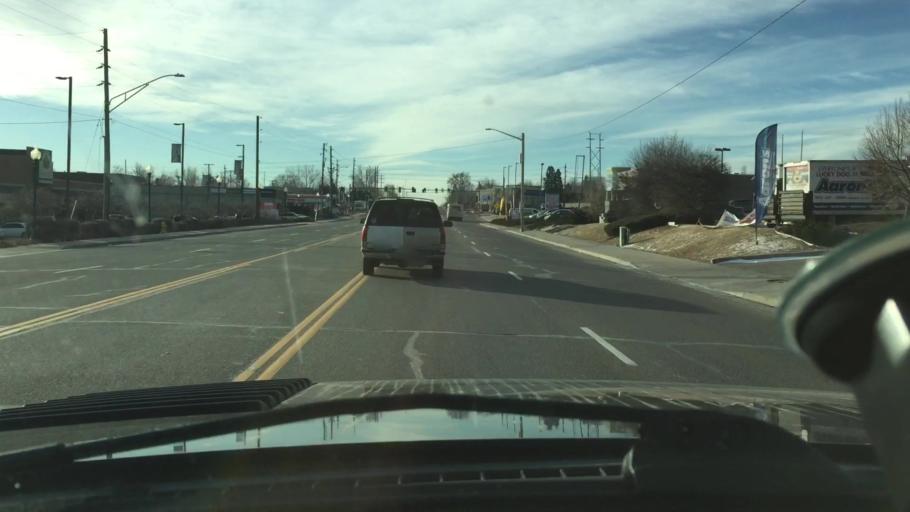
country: US
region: Colorado
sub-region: Adams County
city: Federal Heights
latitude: 39.8511
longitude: -105.0061
